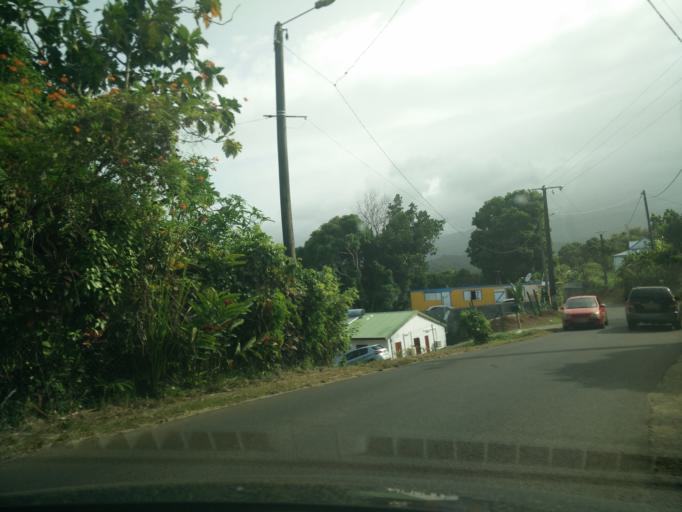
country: GP
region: Guadeloupe
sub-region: Guadeloupe
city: Petit-Bourg
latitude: 16.1284
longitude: -61.5883
